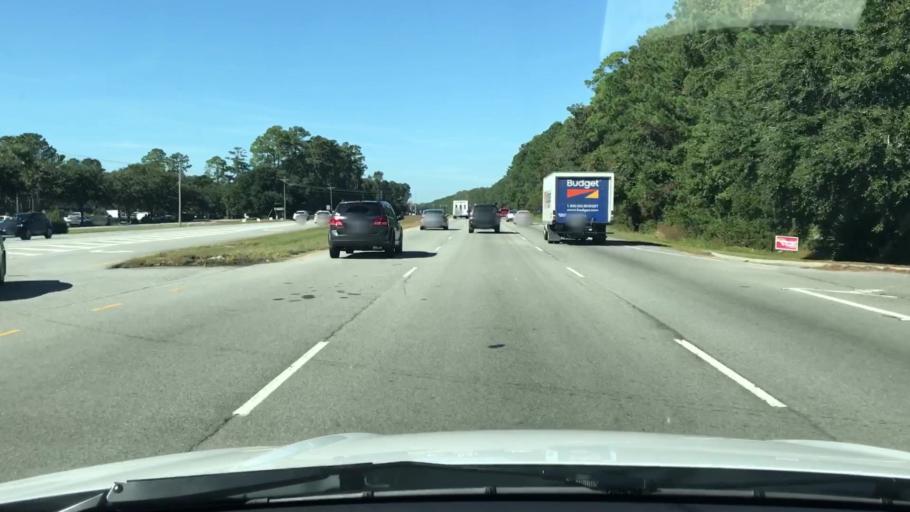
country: US
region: South Carolina
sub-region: Beaufort County
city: Bluffton
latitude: 32.2643
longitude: -80.8566
